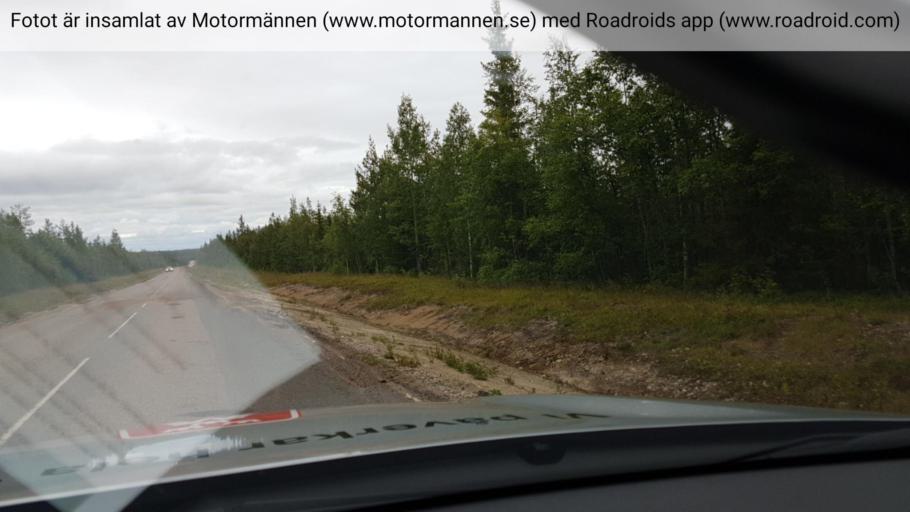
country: SE
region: Norrbotten
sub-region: Overkalix Kommun
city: OEverkalix
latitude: 67.0555
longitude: 22.1923
